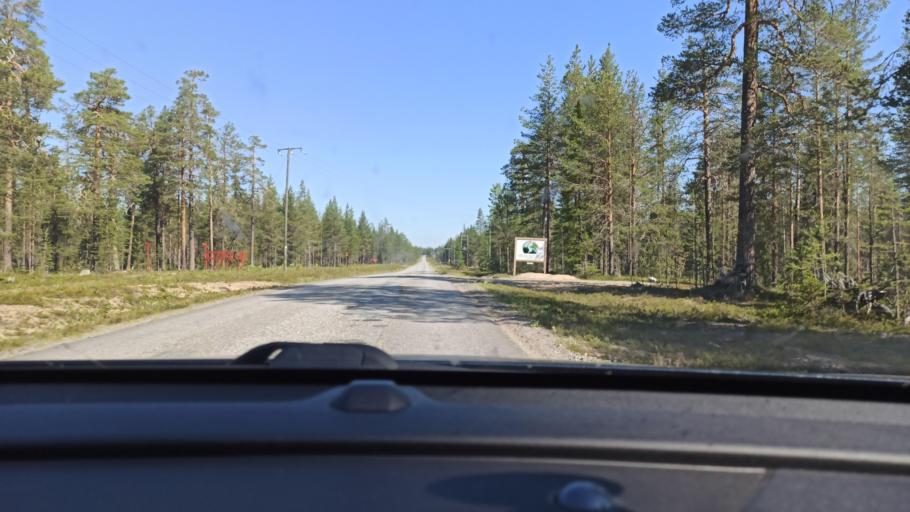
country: FI
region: Lapland
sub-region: Tunturi-Lappi
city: Kolari
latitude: 67.6452
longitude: 24.1597
